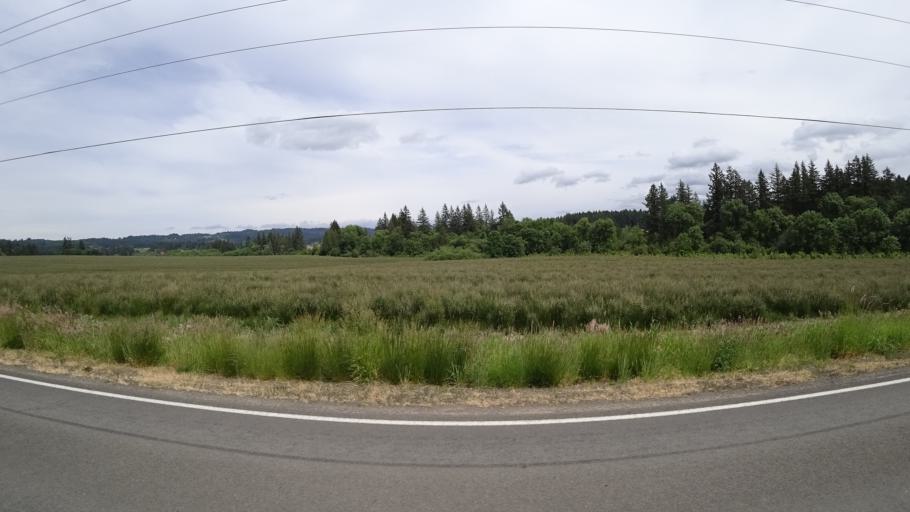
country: US
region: Oregon
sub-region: Washington County
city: Bethany
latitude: 45.5724
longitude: -122.8676
